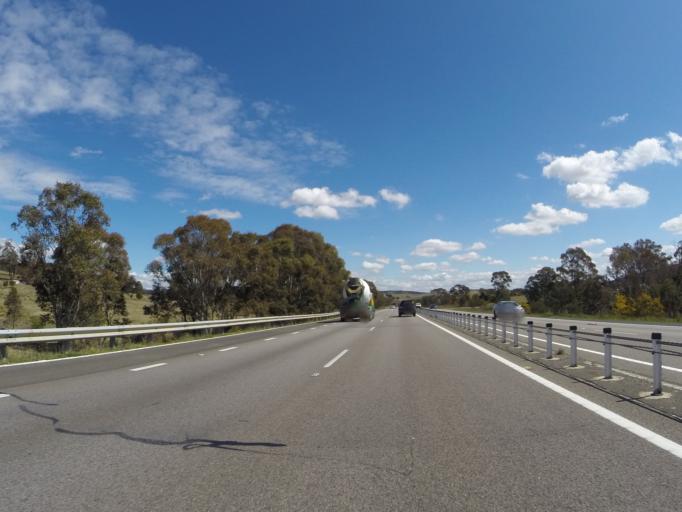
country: AU
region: New South Wales
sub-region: Goulburn Mulwaree
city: Goulburn
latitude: -34.7314
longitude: 149.8182
